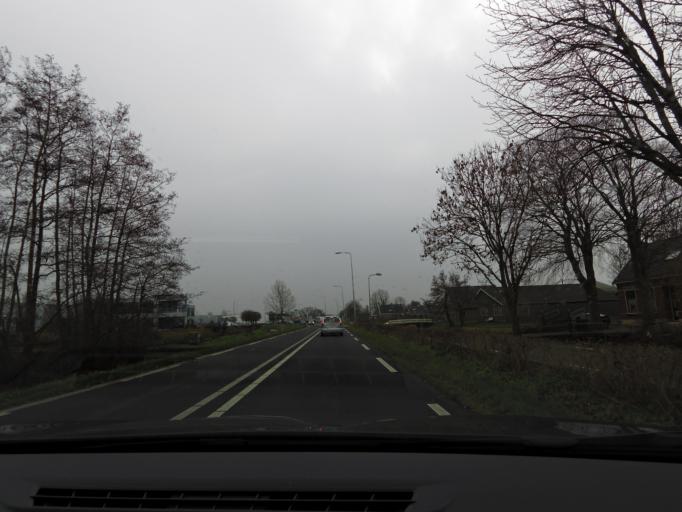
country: NL
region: South Holland
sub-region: Gemeente Nieuwkoop
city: Nieuwkoop
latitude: 52.1649
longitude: 4.7767
